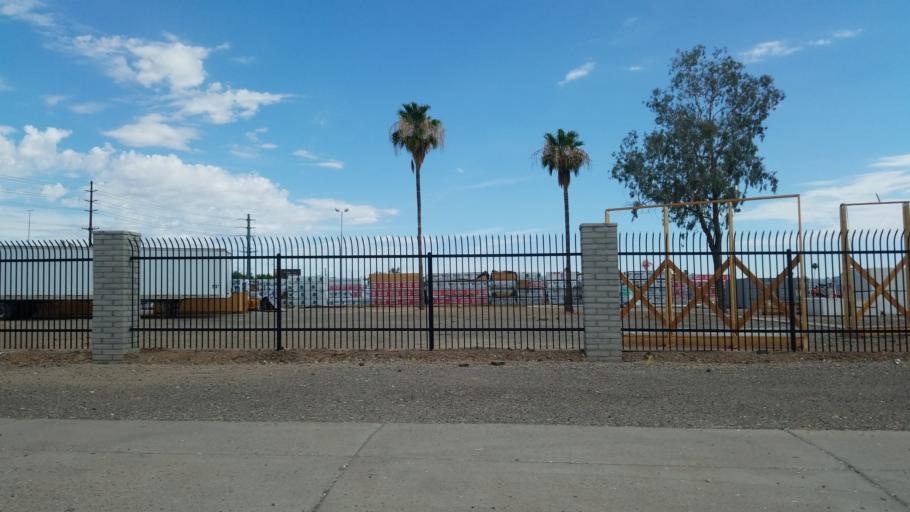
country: US
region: Arizona
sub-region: Maricopa County
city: Glendale
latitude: 33.5529
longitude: -112.2020
